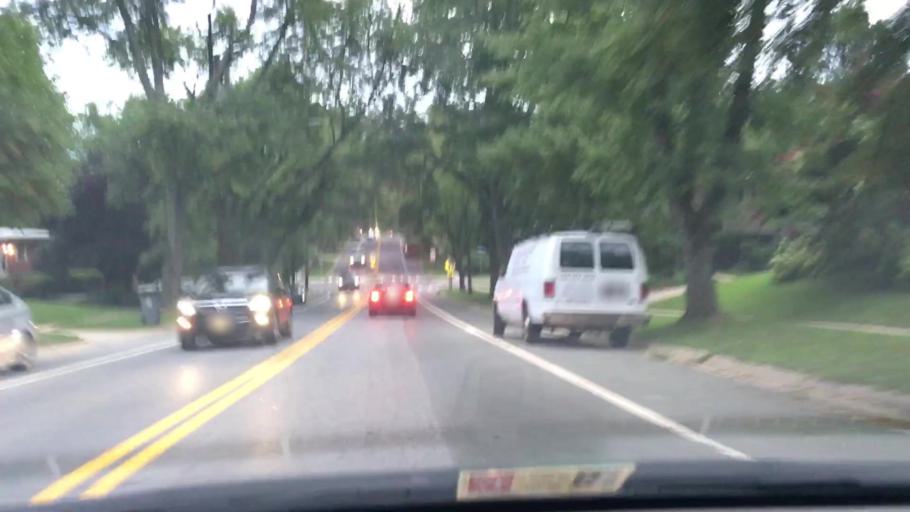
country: US
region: Maryland
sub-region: Montgomery County
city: North Bethesda
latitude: 39.0790
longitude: -77.1128
